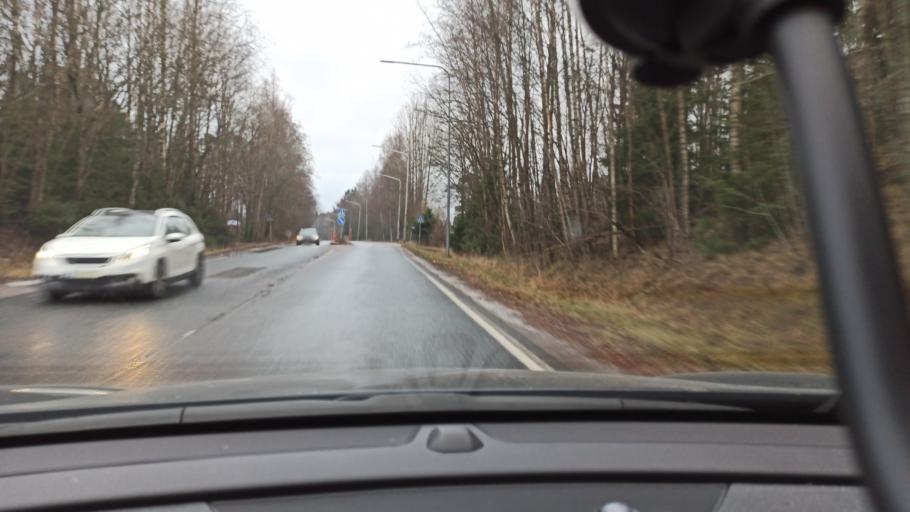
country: FI
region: Uusimaa
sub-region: Helsinki
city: Kirkkonummi
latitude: 60.1377
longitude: 24.4471
